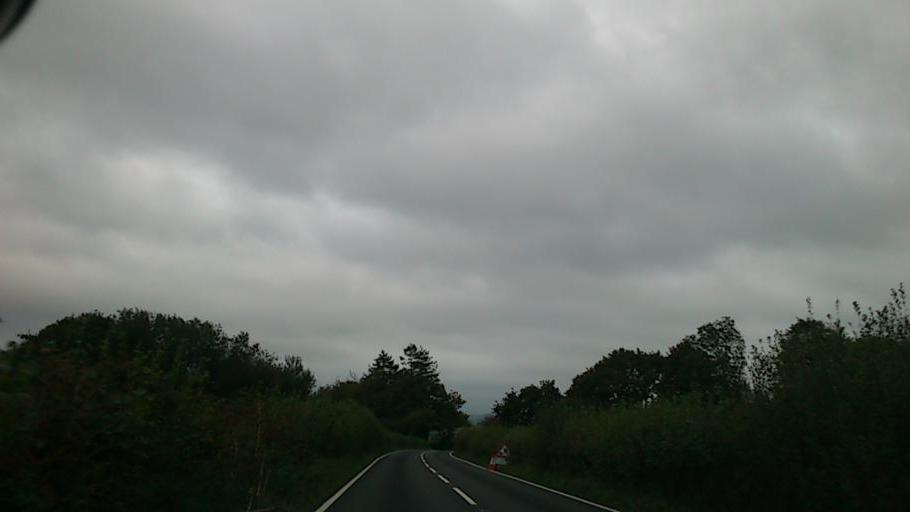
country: GB
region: Wales
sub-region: Sir Powys
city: Machynlleth
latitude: 52.6049
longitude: -3.7916
